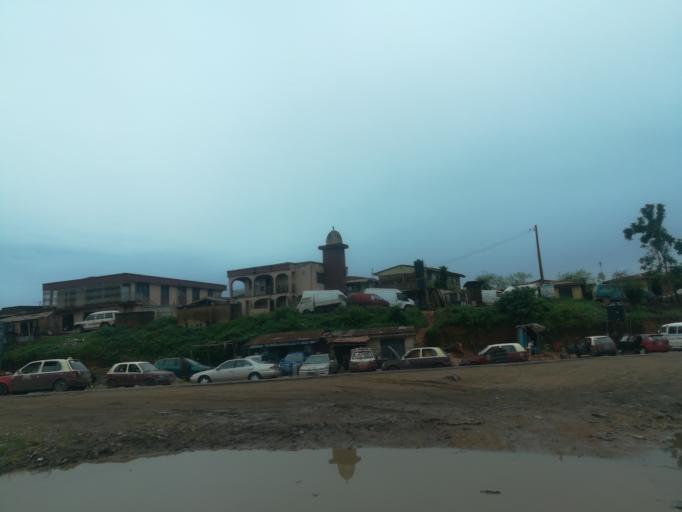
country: NG
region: Oyo
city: Ibadan
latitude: 7.3453
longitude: 3.9186
